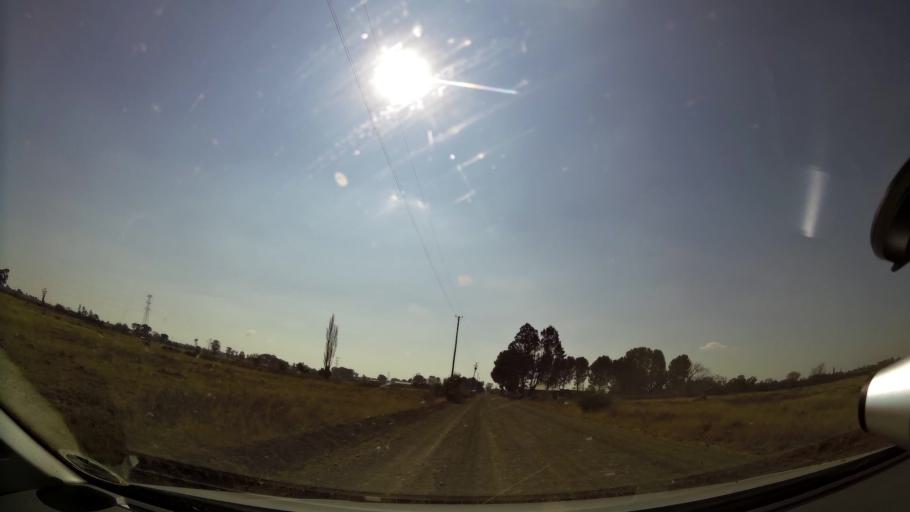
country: ZA
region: Orange Free State
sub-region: Mangaung Metropolitan Municipality
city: Bloemfontein
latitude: -29.1743
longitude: 26.3068
